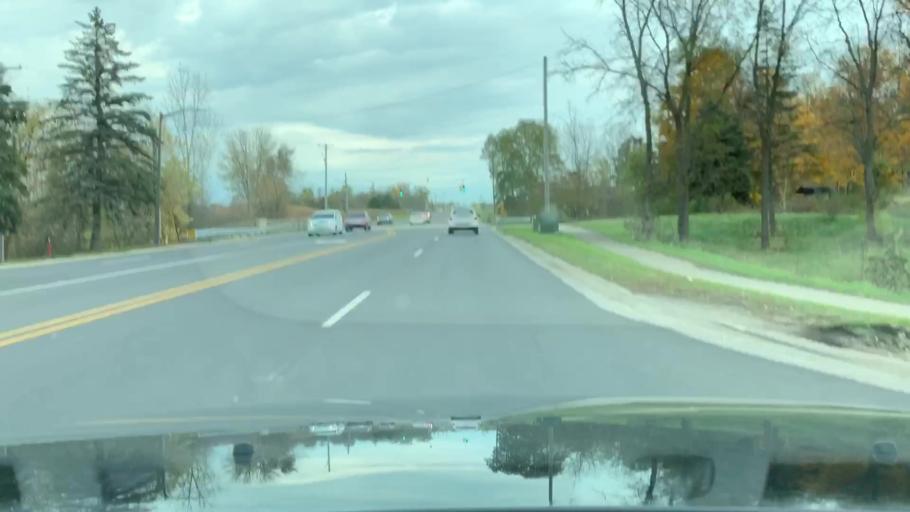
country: US
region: Michigan
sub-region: Ottawa County
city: Zeeland
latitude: 42.7834
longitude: -86.0377
